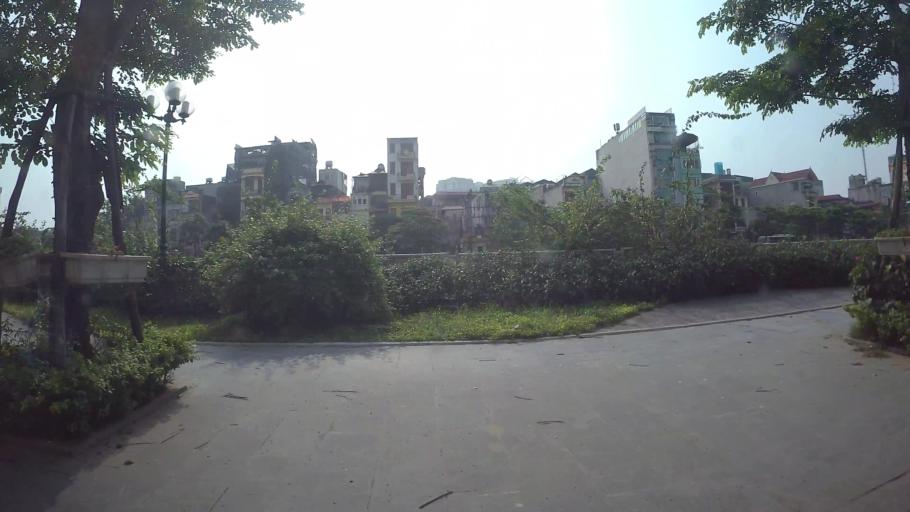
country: VN
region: Ha Noi
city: Thanh Xuan
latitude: 20.9910
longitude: 105.8138
